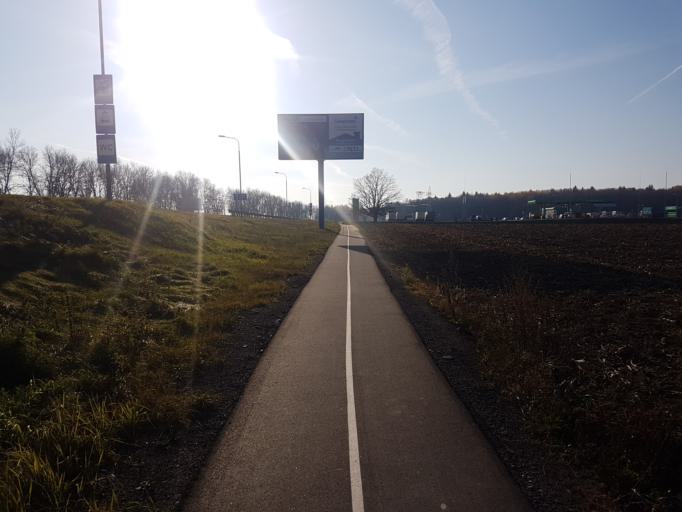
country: BY
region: Minsk
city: Shchomyslitsa
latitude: 53.8182
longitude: 27.4318
